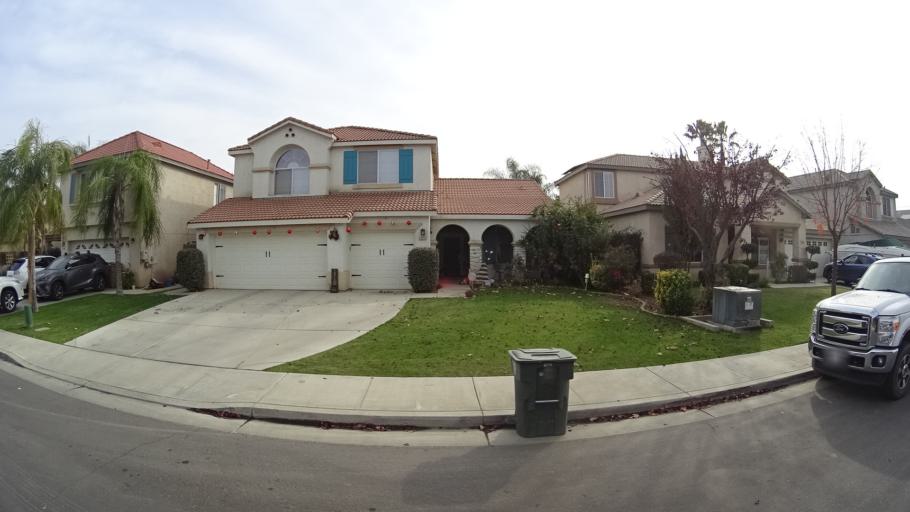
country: US
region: California
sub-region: Kern County
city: Rosedale
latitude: 35.3424
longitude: -119.1443
